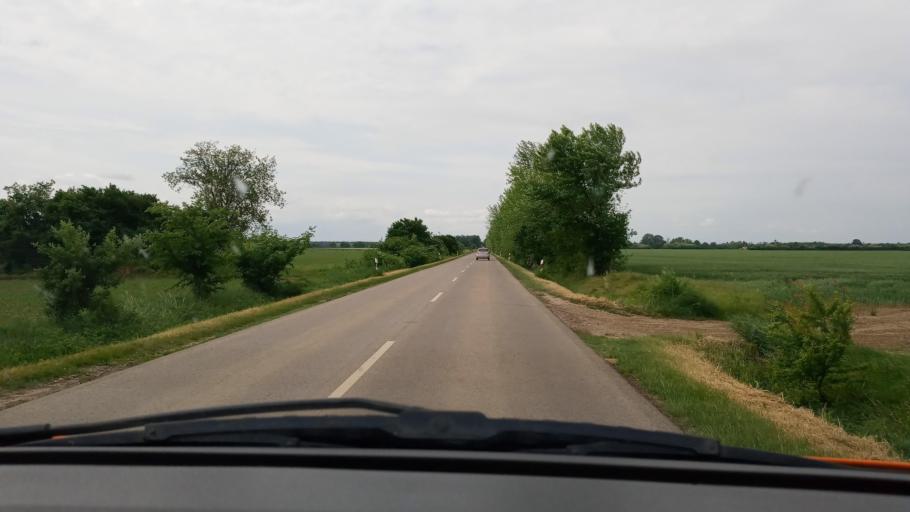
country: HU
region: Baranya
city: Vajszlo
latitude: 45.9168
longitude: 18.0547
